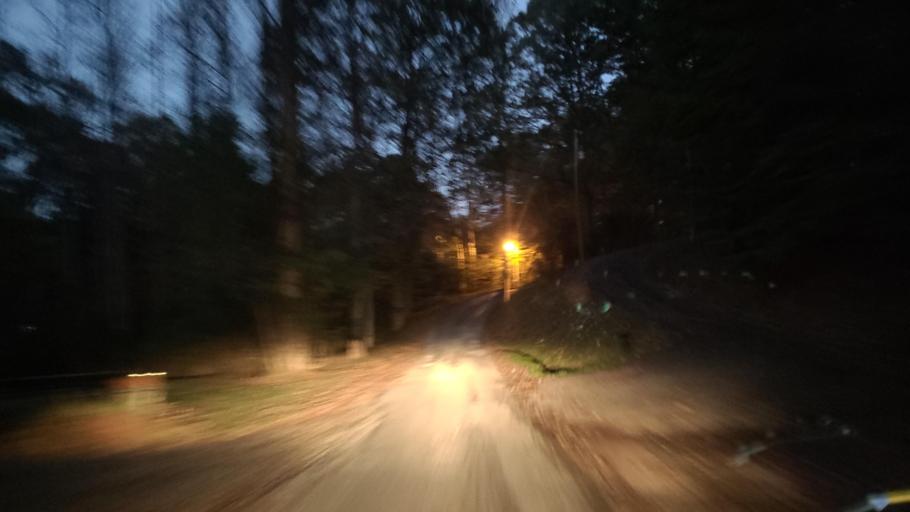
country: US
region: Georgia
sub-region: Union County
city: Blairsville
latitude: 34.9633
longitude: -83.8961
